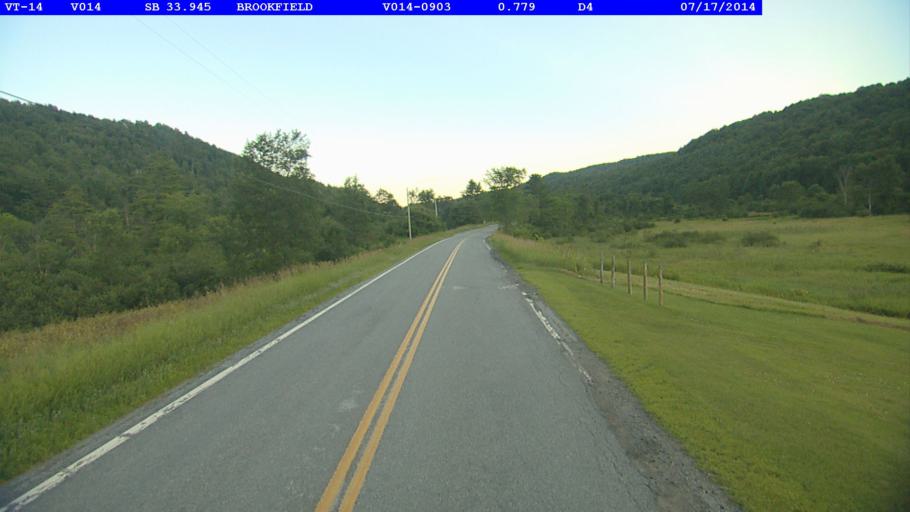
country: US
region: Vermont
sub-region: Orange County
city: Chelsea
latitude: 43.9902
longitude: -72.5561
